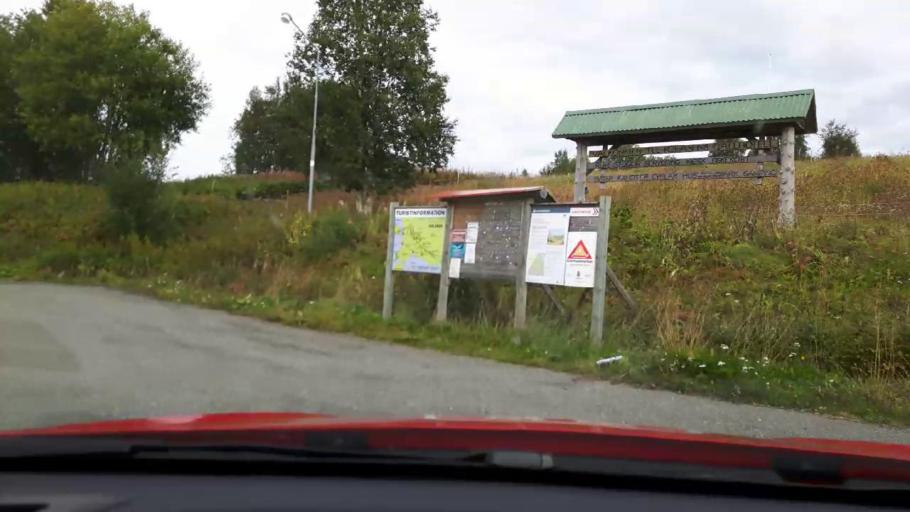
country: SE
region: Jaemtland
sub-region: Are Kommun
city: Are
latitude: 63.7507
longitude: 12.9589
